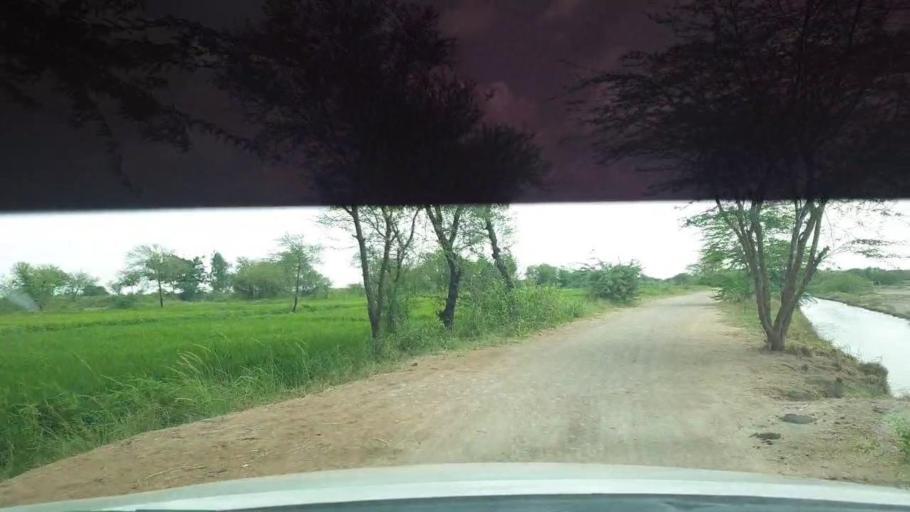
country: PK
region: Sindh
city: Kadhan
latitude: 24.6213
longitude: 69.0324
